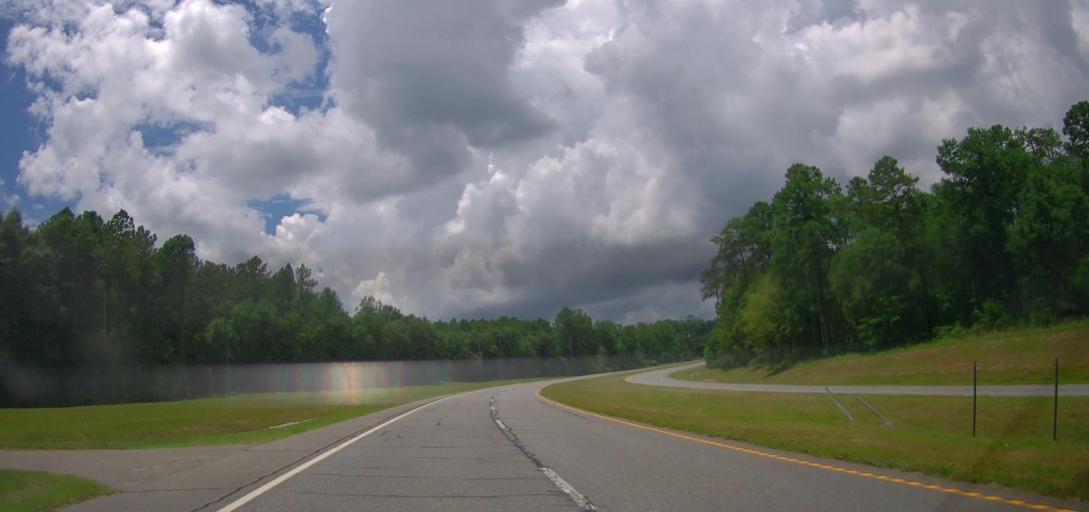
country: US
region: Georgia
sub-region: Pulaski County
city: Hawkinsville
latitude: 32.2622
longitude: -83.4075
